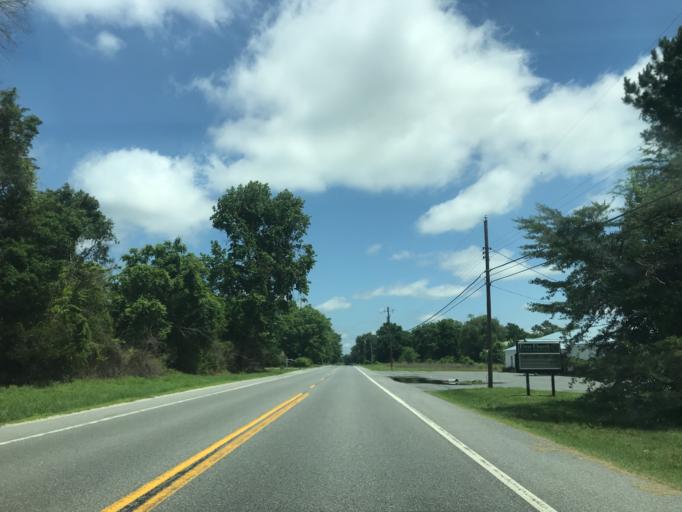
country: US
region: Maryland
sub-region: Caroline County
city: Federalsburg
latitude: 38.6989
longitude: -75.7609
